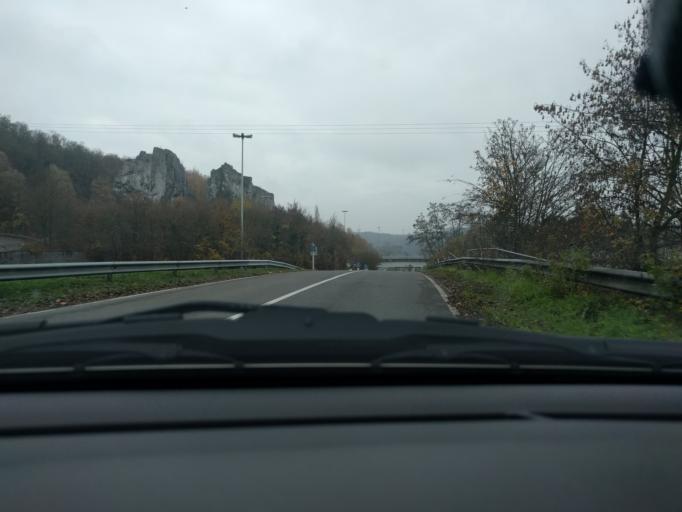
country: BE
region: Wallonia
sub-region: Province de Namur
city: Namur
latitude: 50.4682
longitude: 4.8966
